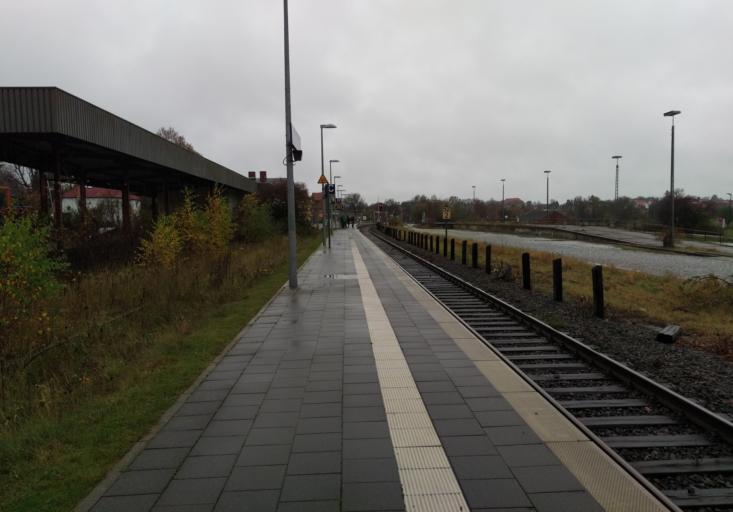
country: DE
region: Schleswig-Holstein
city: Oldenburg in Holstein
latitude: 54.2830
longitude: 10.8832
